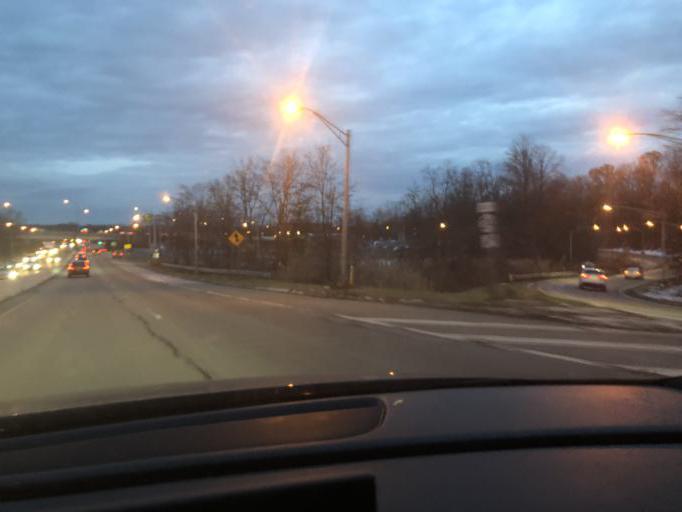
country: US
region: New Jersey
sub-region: Morris County
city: Madison
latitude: 40.7926
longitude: -74.4308
